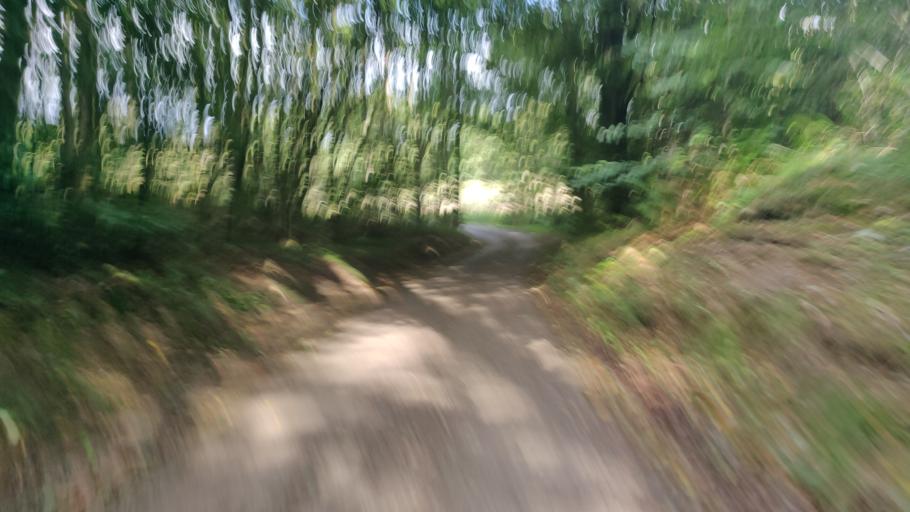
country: DK
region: South Denmark
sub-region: Kolding Kommune
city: Lunderskov
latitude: 55.5483
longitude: 9.3493
